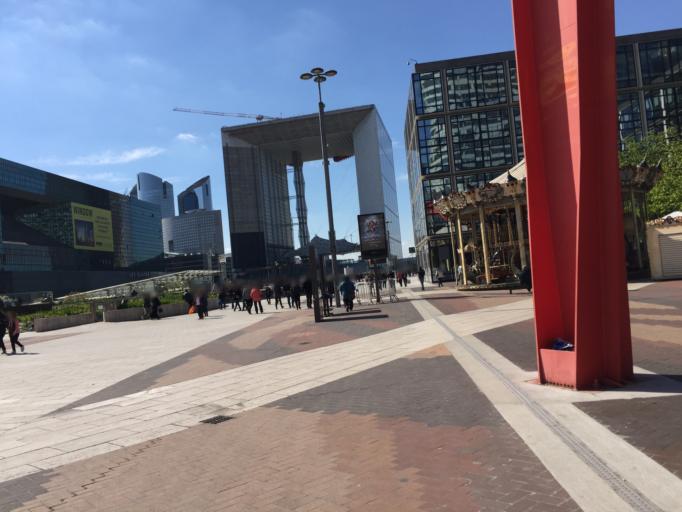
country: FR
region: Ile-de-France
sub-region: Departement des Hauts-de-Seine
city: La Defense
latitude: 48.8912
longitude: 2.2418
